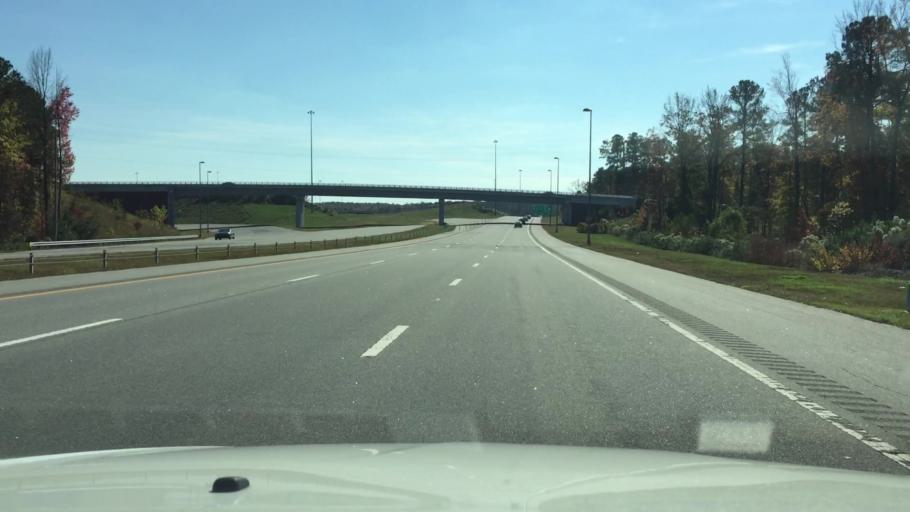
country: US
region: North Carolina
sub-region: Wake County
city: Morrisville
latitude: 35.8608
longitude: -78.8641
